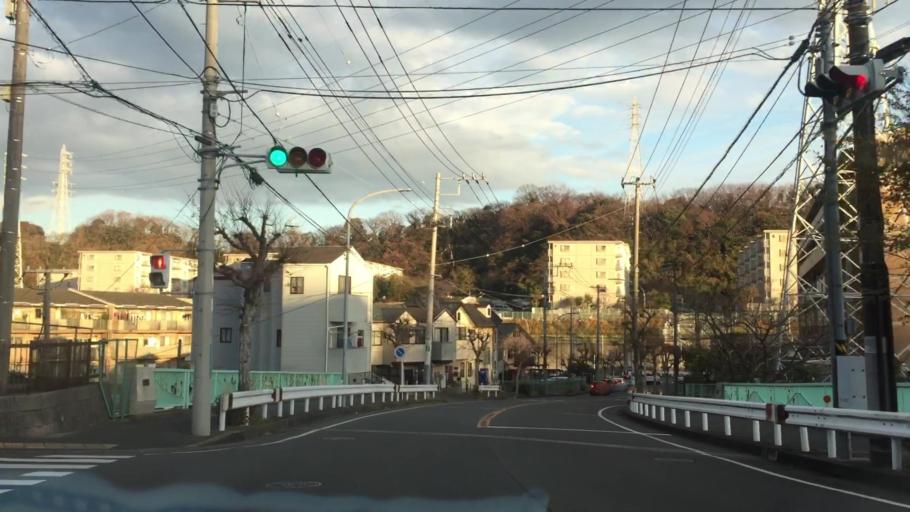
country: JP
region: Kanagawa
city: Zushi
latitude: 35.3393
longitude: 139.6089
